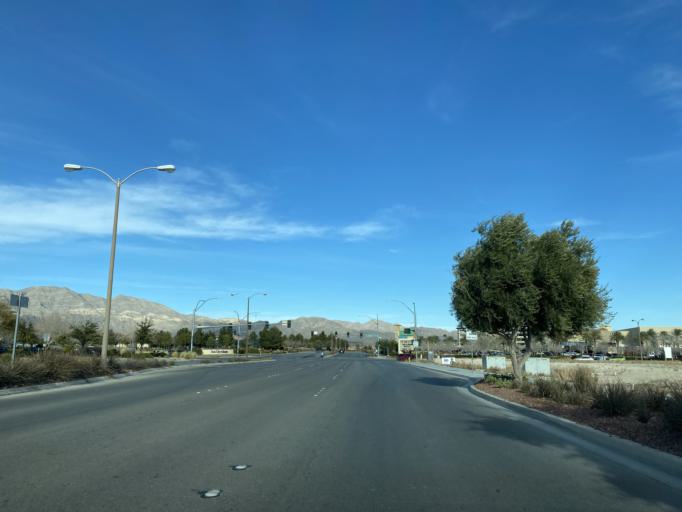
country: US
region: Nevada
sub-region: Clark County
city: North Las Vegas
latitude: 36.2919
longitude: -115.1846
